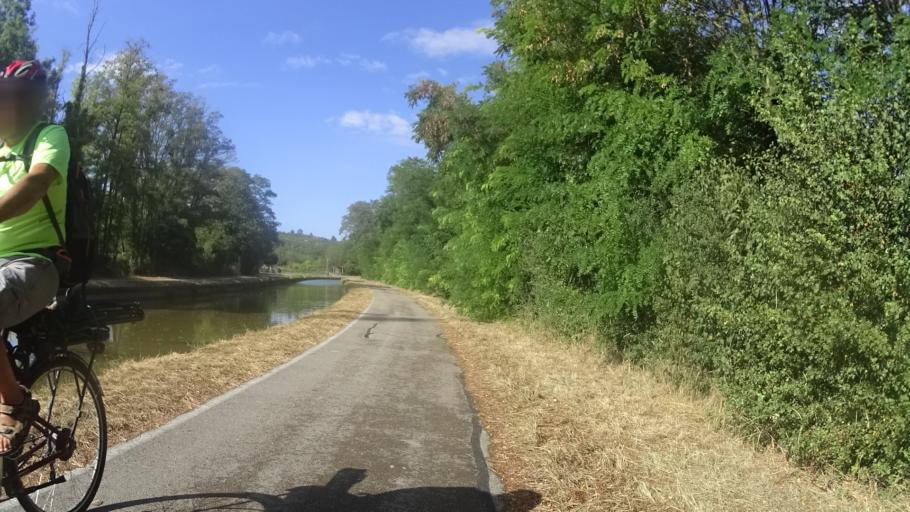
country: FR
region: Bourgogne
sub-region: Departement de Saone-et-Loire
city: Chagny
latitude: 46.9086
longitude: 4.7310
